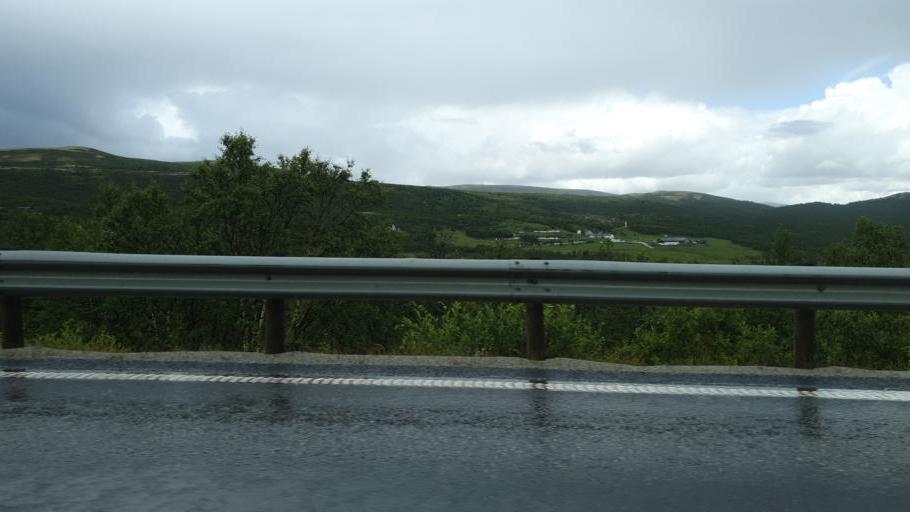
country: NO
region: Oppland
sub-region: Dovre
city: Dovre
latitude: 62.2137
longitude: 9.5566
